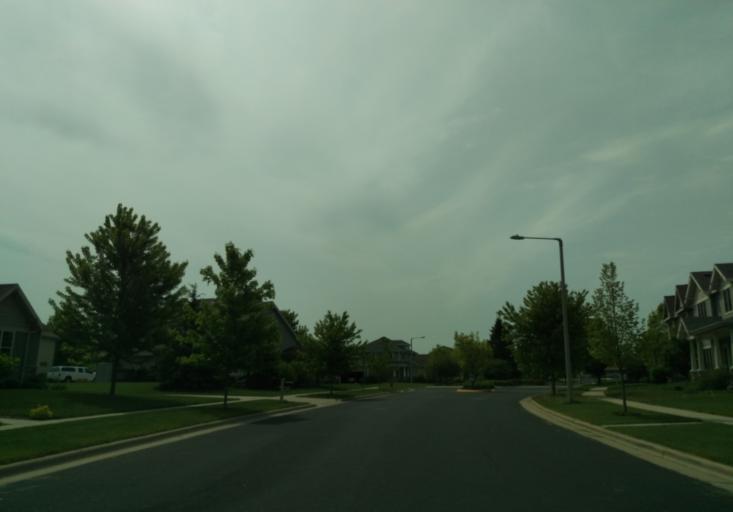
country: US
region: Wisconsin
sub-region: Dane County
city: Monona
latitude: 43.0877
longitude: -89.2738
